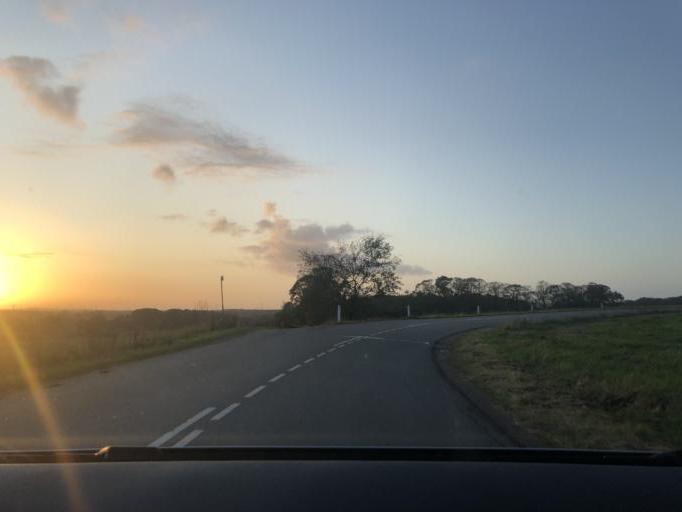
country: DK
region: Capital Region
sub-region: Egedal Kommune
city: Stenlose
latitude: 55.8026
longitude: 12.2128
